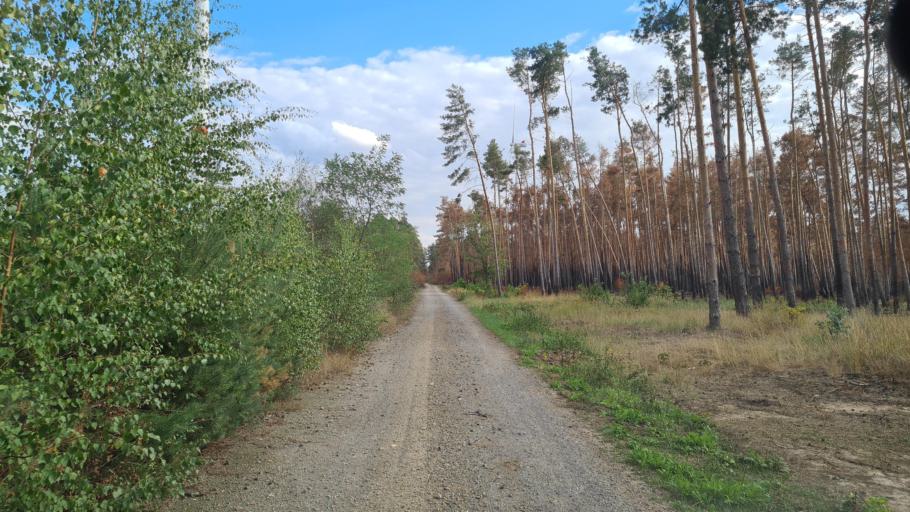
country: DE
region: Saxony
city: Arzberg
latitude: 51.5649
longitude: 13.1815
